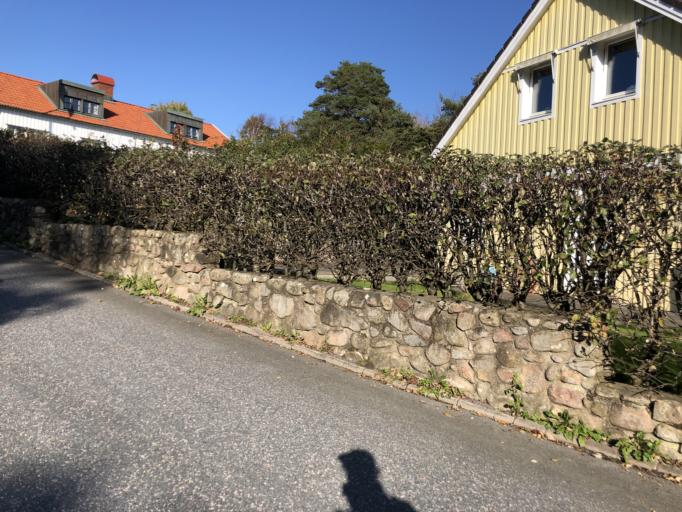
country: SE
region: Vaestra Goetaland
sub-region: Goteborg
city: Billdal
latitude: 57.6220
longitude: 11.8944
